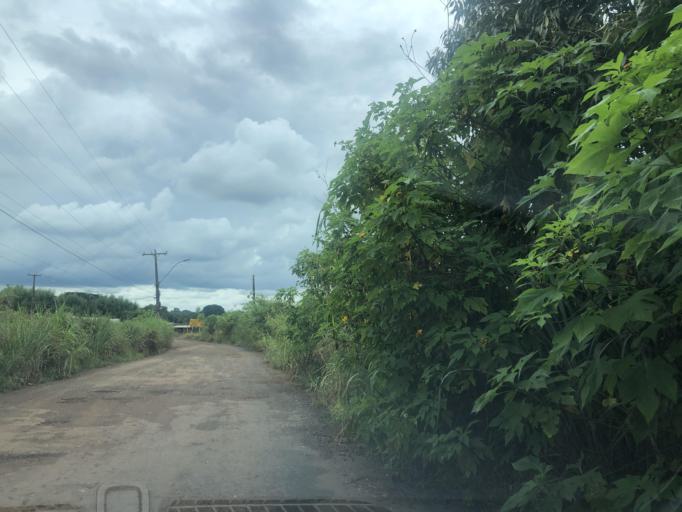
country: BR
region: Federal District
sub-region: Brasilia
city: Brasilia
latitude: -15.9336
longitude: -47.9383
